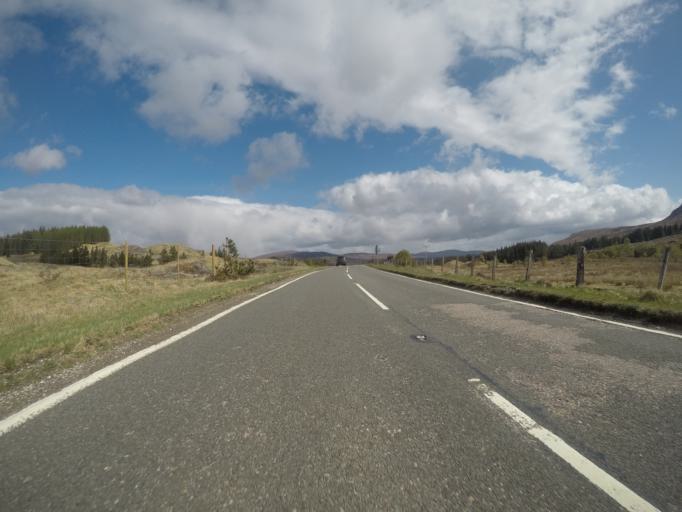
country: GB
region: Scotland
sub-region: Highland
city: Spean Bridge
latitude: 57.1371
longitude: -4.9546
